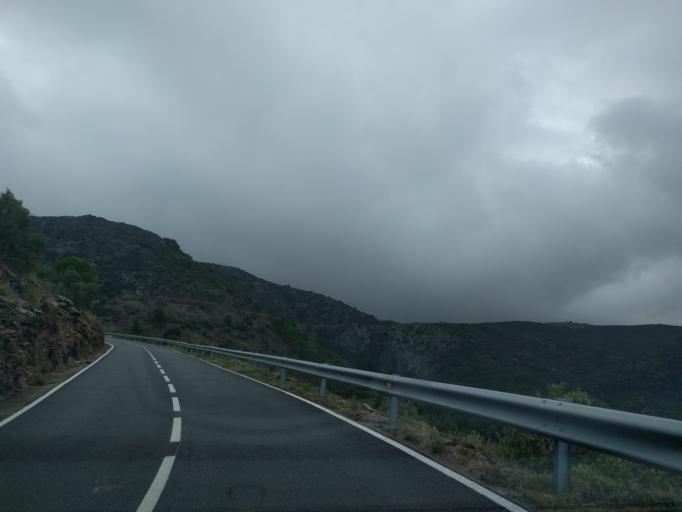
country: ES
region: Catalonia
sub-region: Provincia de Girona
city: Cadaques
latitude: 42.3062
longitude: 3.2227
